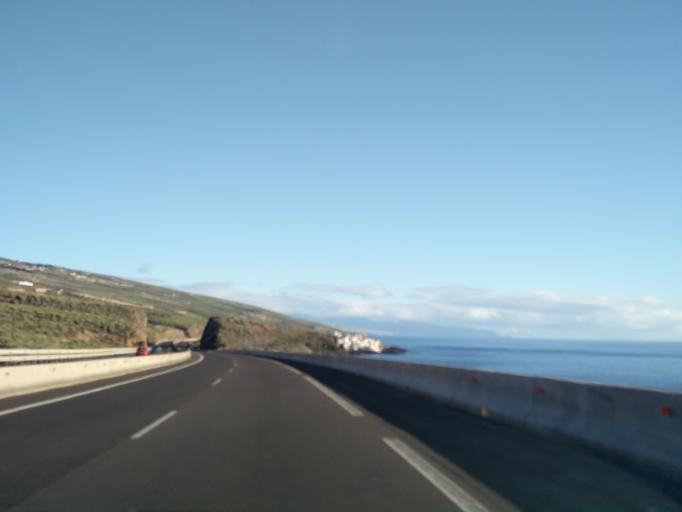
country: ES
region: Canary Islands
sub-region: Provincia de Santa Cruz de Tenerife
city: Fasnia
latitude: 28.2290
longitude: -16.4100
